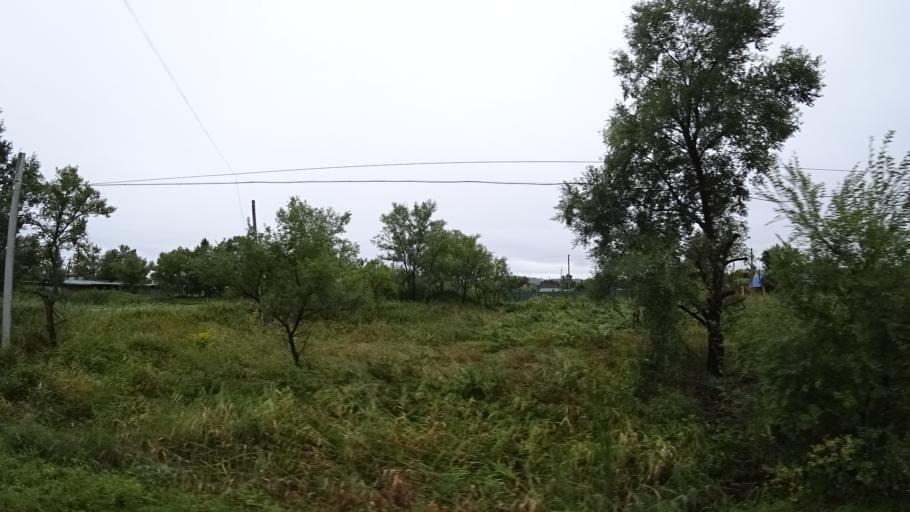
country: RU
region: Primorskiy
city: Monastyrishche
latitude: 44.2038
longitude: 132.4552
